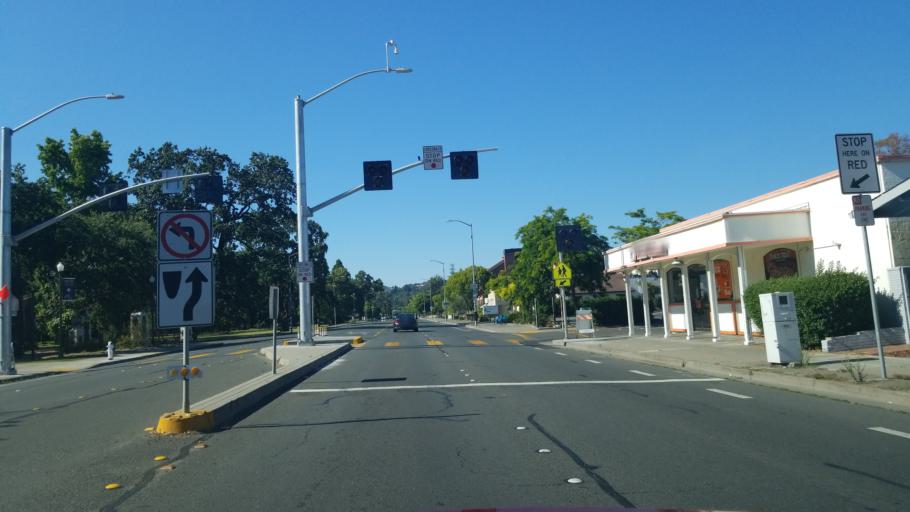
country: US
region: California
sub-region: Sonoma County
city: Santa Rosa
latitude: 38.4544
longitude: -122.7174
